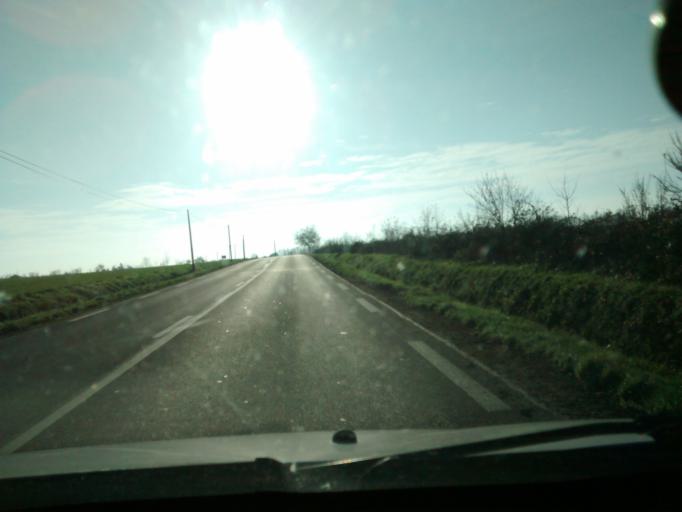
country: FR
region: Brittany
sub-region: Departement d'Ille-et-Vilaine
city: Tremblay
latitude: 48.4076
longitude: -1.4820
